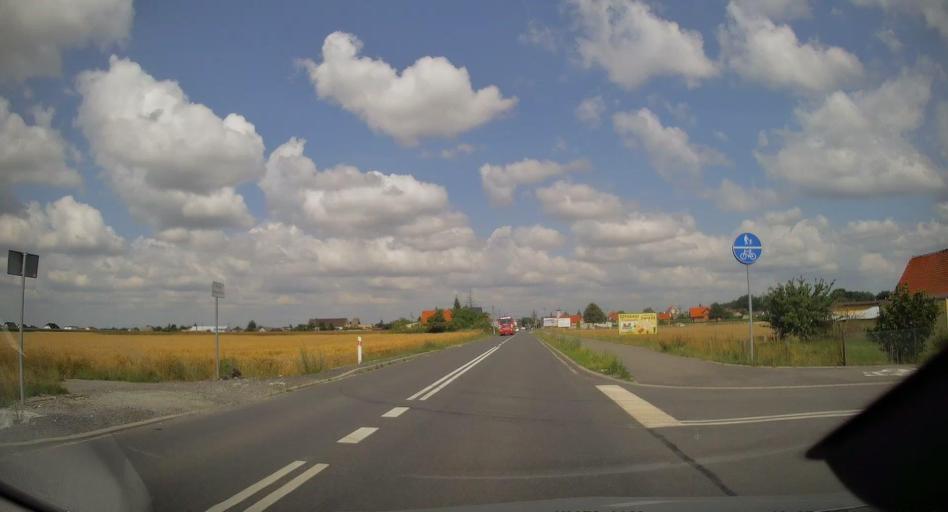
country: PL
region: Opole Voivodeship
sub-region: Powiat kedzierzynsko-kozielski
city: Wiekszyce
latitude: 50.3326
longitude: 18.1068
